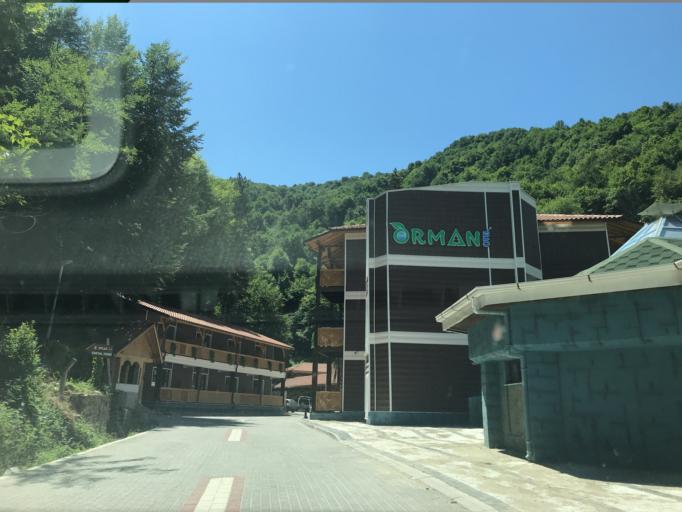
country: TR
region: Bursa
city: Tahtakopru
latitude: 39.9279
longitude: 29.5881
